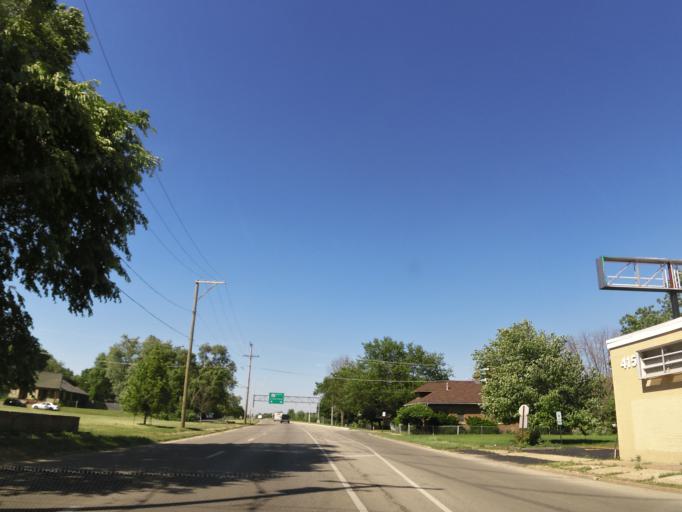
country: US
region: Illinois
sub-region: Winnebago County
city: Rockford
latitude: 42.2700
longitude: -89.0838
